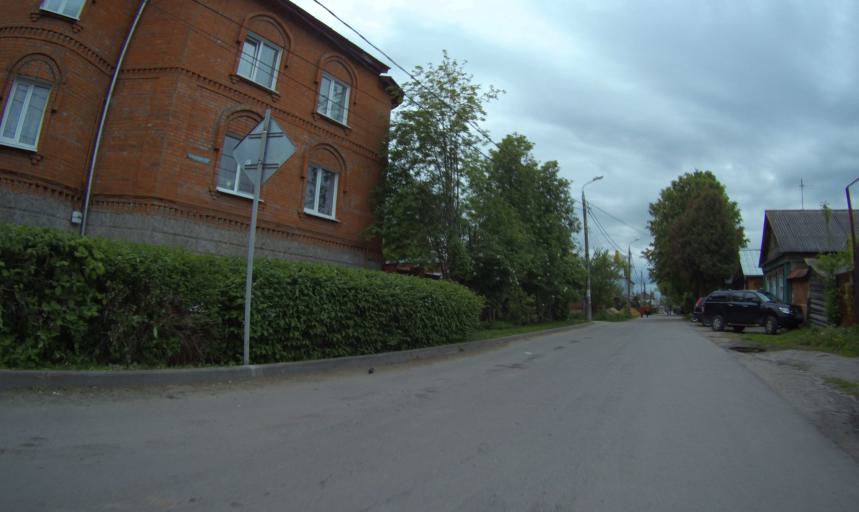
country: RU
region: Moskovskaya
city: Kolomna
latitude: 55.0985
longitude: 38.7701
